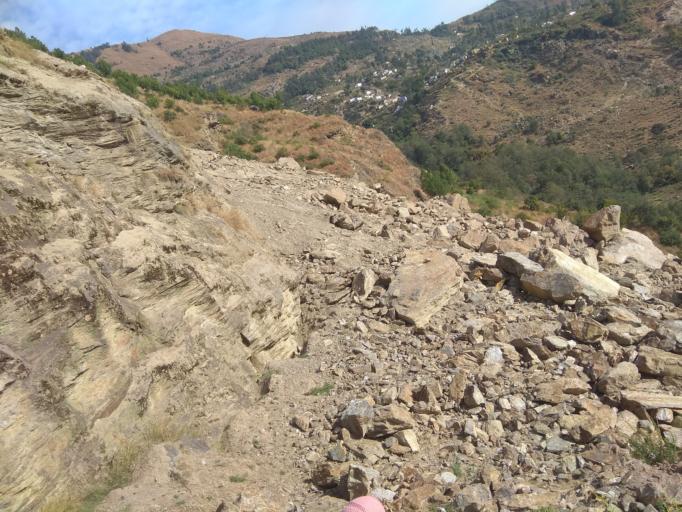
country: NP
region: Mid Western
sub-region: Bheri Zone
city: Dailekh
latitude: 29.2383
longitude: 81.6514
